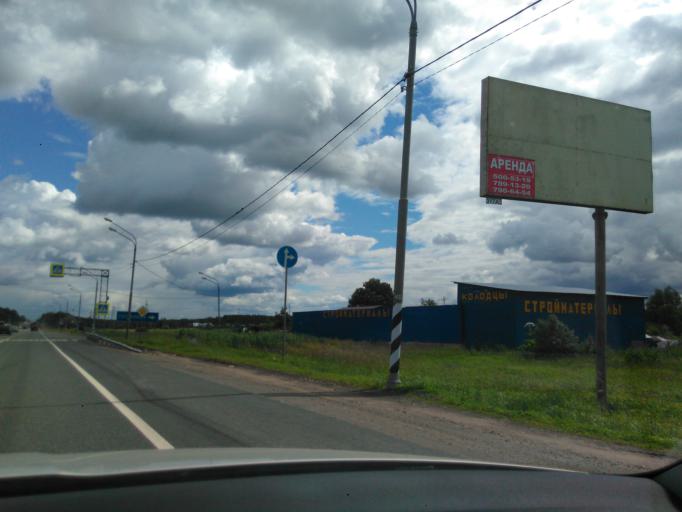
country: RU
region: Moskovskaya
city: Solnechnogorsk
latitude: 56.2287
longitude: 36.9110
